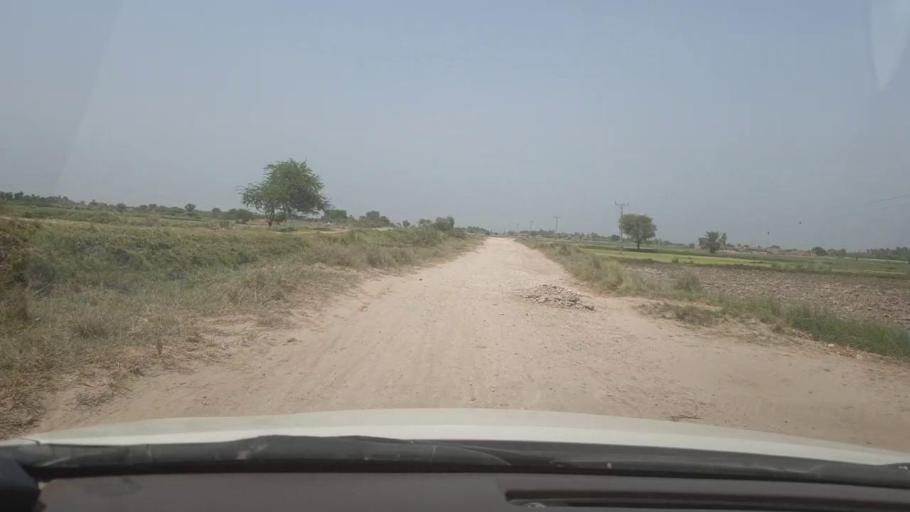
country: PK
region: Sindh
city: Shikarpur
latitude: 27.9372
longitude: 68.5754
